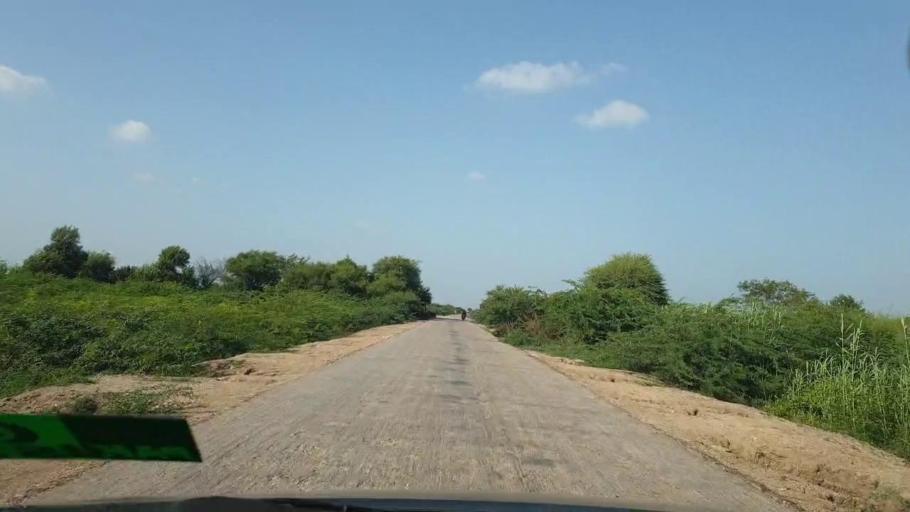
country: PK
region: Sindh
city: Tando Bago
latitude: 24.7107
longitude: 69.1926
